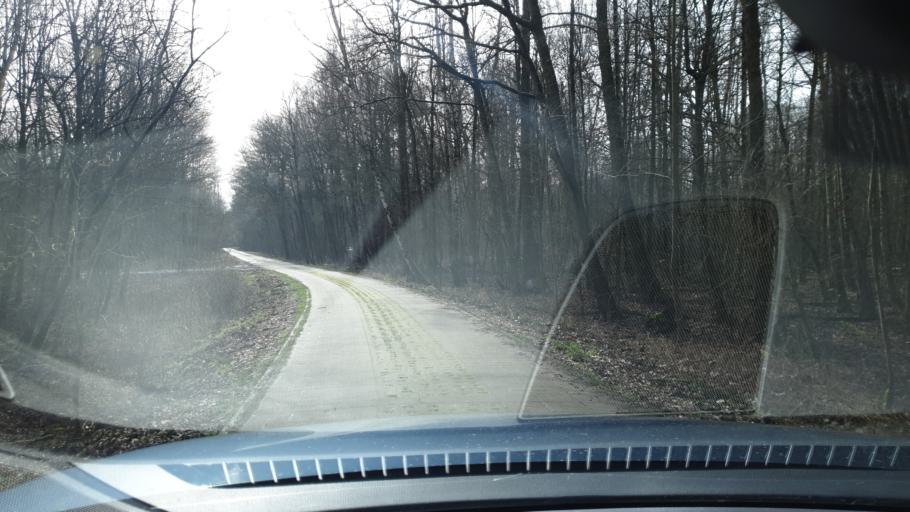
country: DE
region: Saxony-Anhalt
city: Vockerode
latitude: 51.8258
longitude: 12.3402
